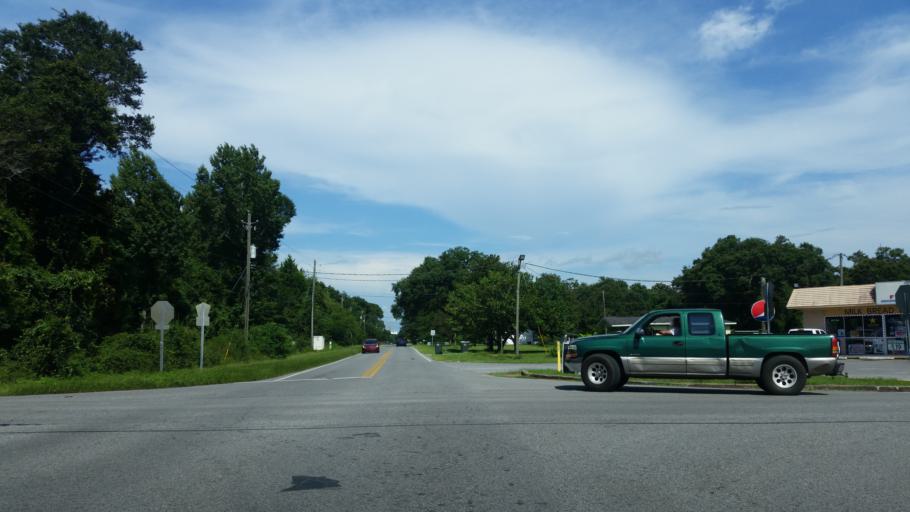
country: US
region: Florida
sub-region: Santa Rosa County
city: Pace
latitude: 30.5901
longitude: -87.1618
